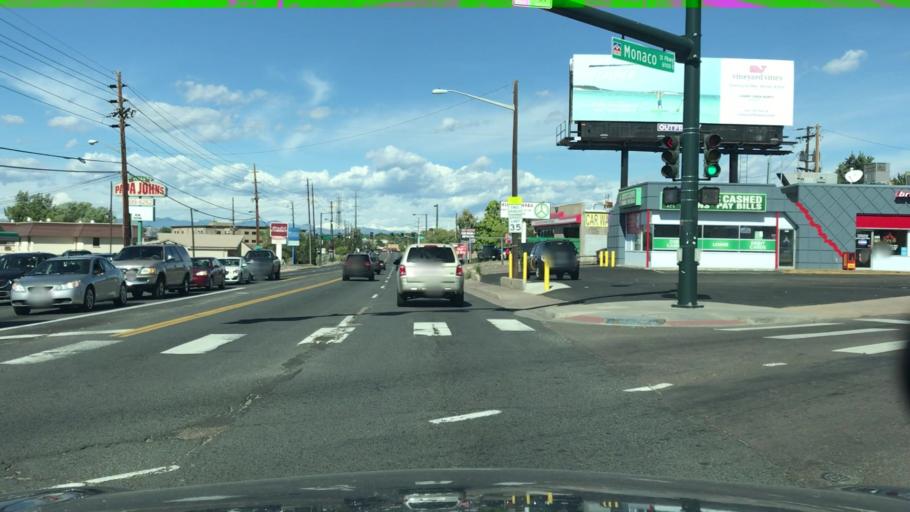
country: US
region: Colorado
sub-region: Arapahoe County
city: Glendale
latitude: 39.7030
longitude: -104.9129
